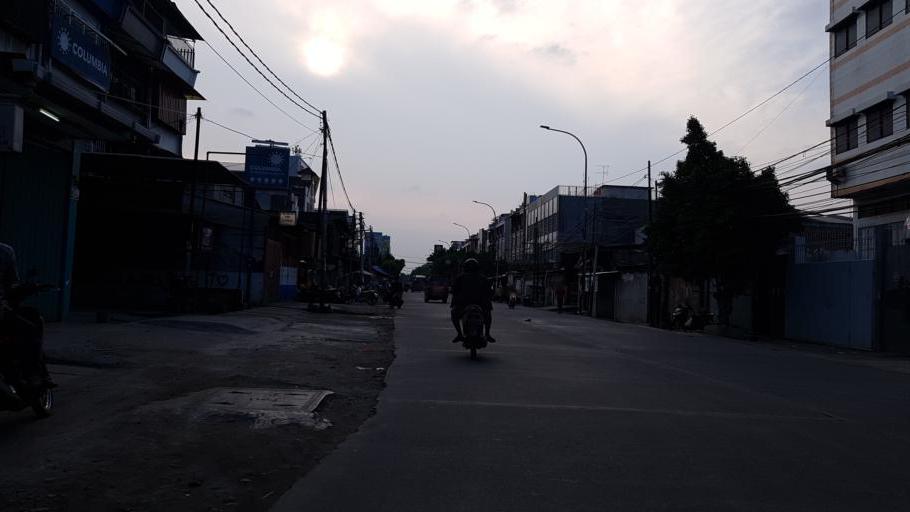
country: ID
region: Jakarta Raya
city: Jakarta
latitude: -6.1380
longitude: 106.7851
